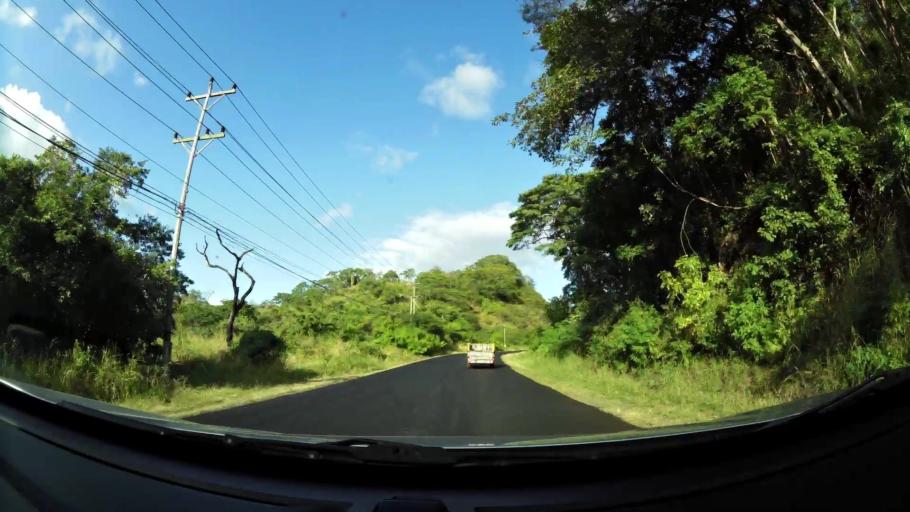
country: CR
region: Guanacaste
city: Sardinal
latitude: 10.5381
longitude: -85.6729
